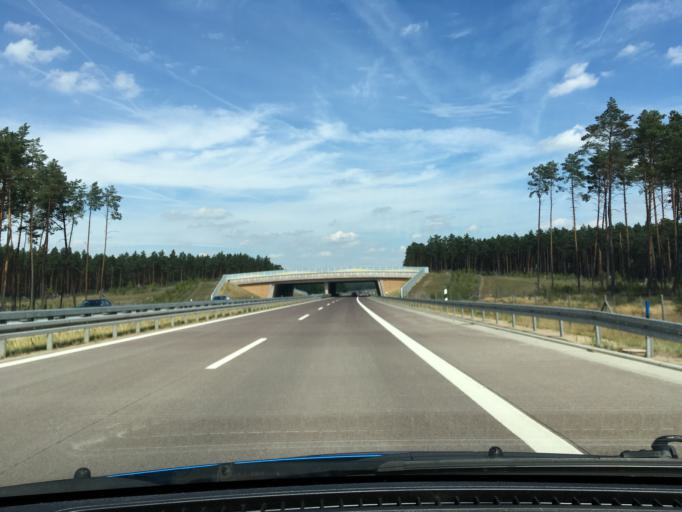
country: DE
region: Mecklenburg-Vorpommern
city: Gross Laasch
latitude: 53.3682
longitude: 11.5170
